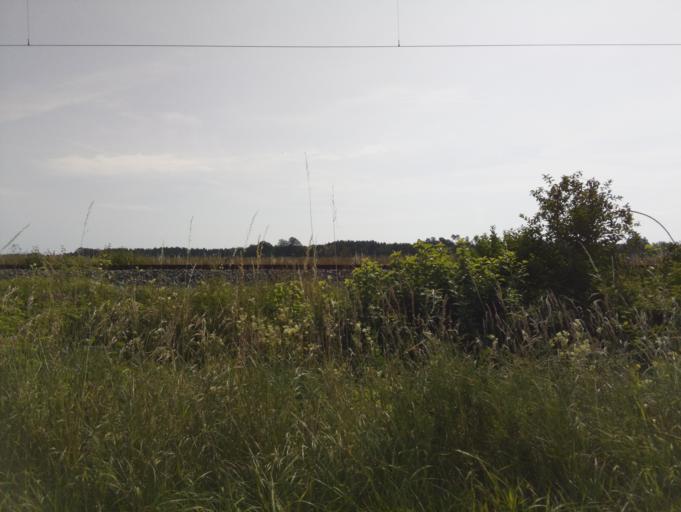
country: CH
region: Zurich
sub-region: Bezirk Andelfingen
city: Henggart
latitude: 47.5714
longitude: 8.6824
